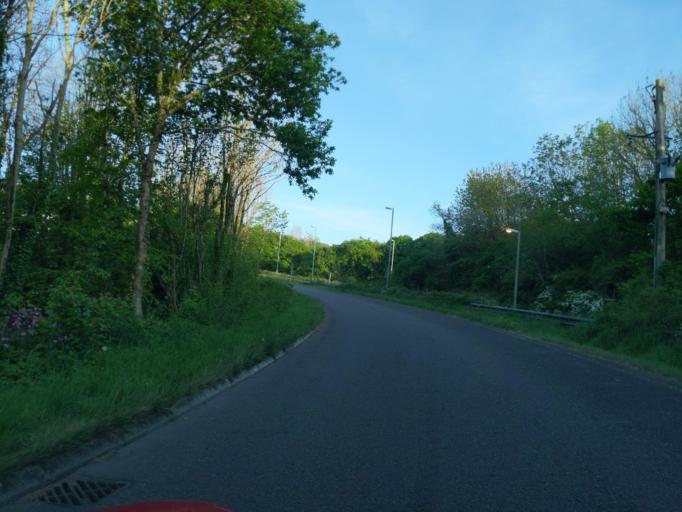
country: GB
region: England
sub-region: Cornwall
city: Saltash
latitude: 50.4147
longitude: -4.2459
